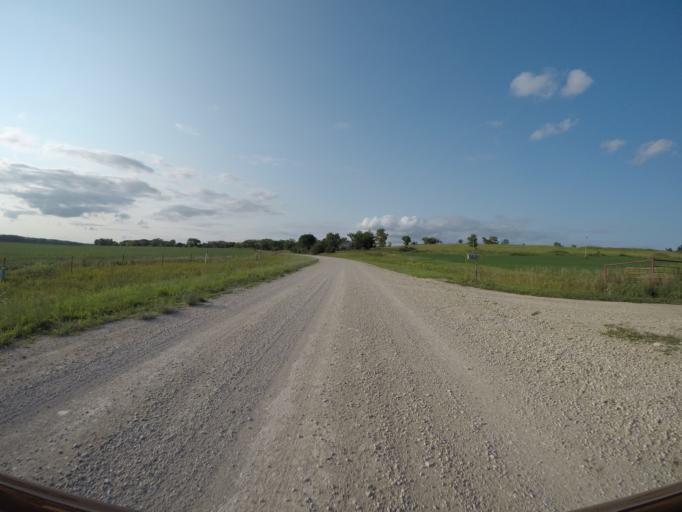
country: US
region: Kansas
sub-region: Wabaunsee County
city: Alma
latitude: 38.9616
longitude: -96.2520
